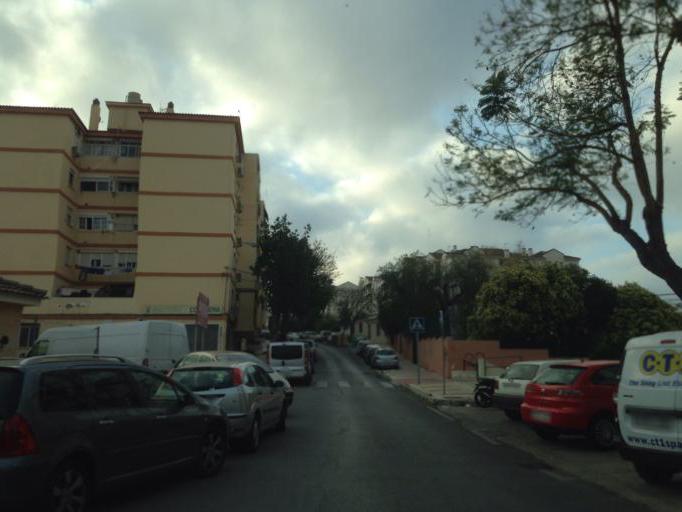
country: ES
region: Andalusia
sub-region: Provincia de Malaga
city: Malaga
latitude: 36.7469
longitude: -4.4201
